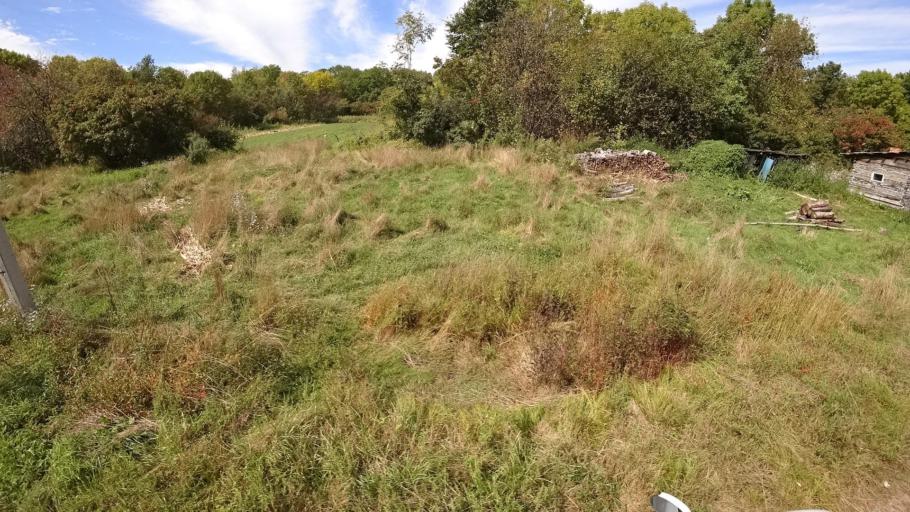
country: RU
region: Primorskiy
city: Yakovlevka
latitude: 44.7119
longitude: 133.6298
